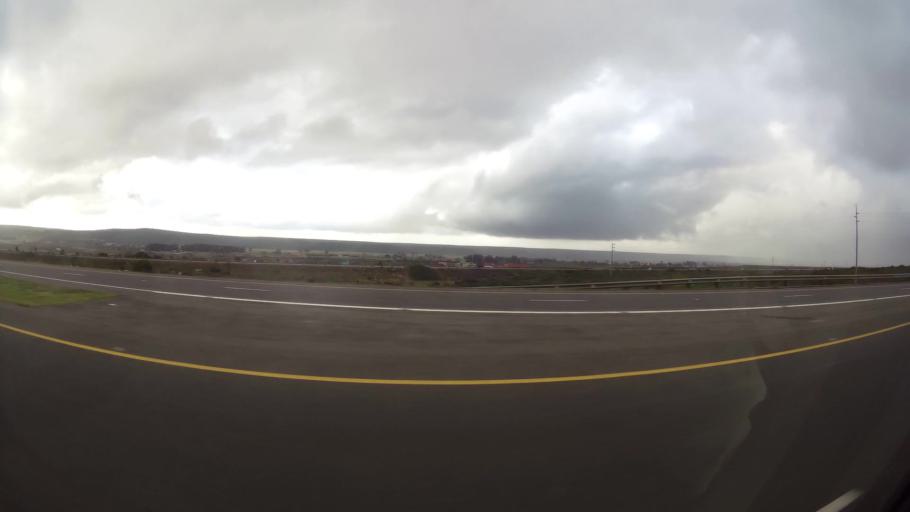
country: ZA
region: Eastern Cape
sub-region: Nelson Mandela Bay Metropolitan Municipality
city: Uitenhage
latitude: -33.8168
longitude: 25.5004
